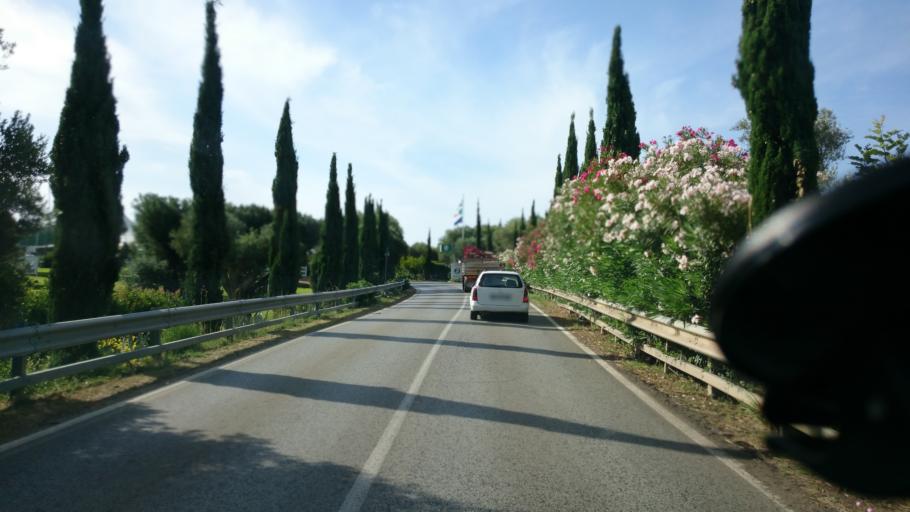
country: IT
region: Campania
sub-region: Provincia di Salerno
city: Marina di Camerota
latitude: 40.0078
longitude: 15.3534
